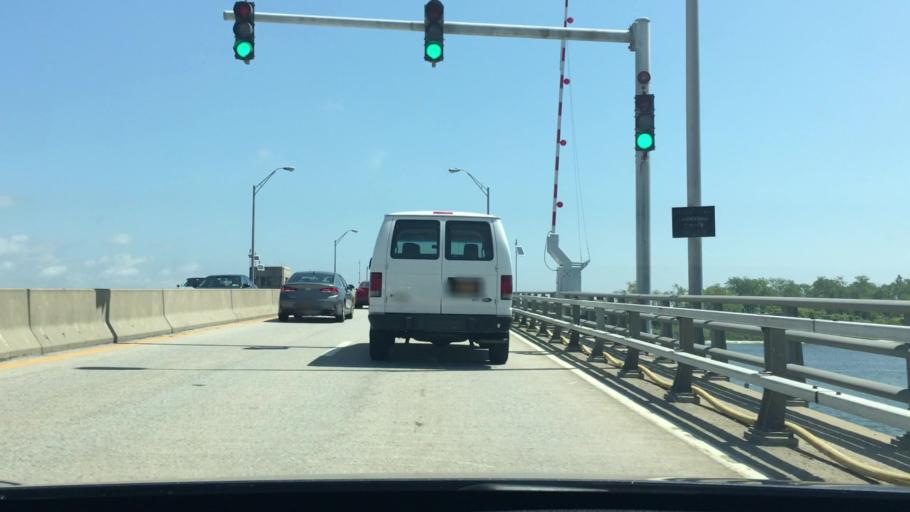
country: US
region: New York
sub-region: Nassau County
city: Point Lookout
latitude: 40.6043
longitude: -73.5707
